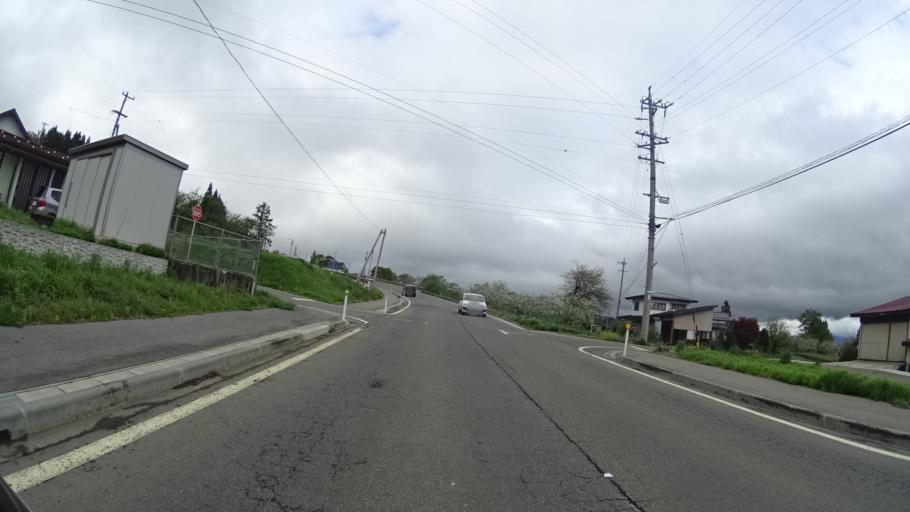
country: JP
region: Nagano
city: Nagano-shi
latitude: 36.7396
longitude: 138.2055
